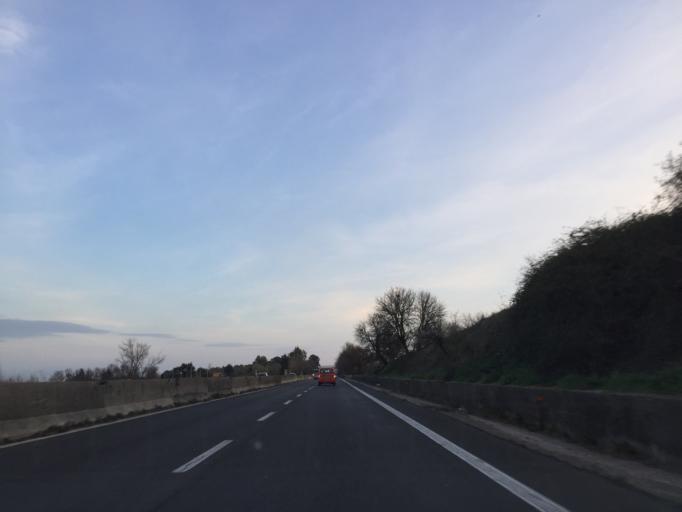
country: IT
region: Latium
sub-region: Citta metropolitana di Roma Capitale
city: Formello
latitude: 42.0271
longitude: 12.4318
